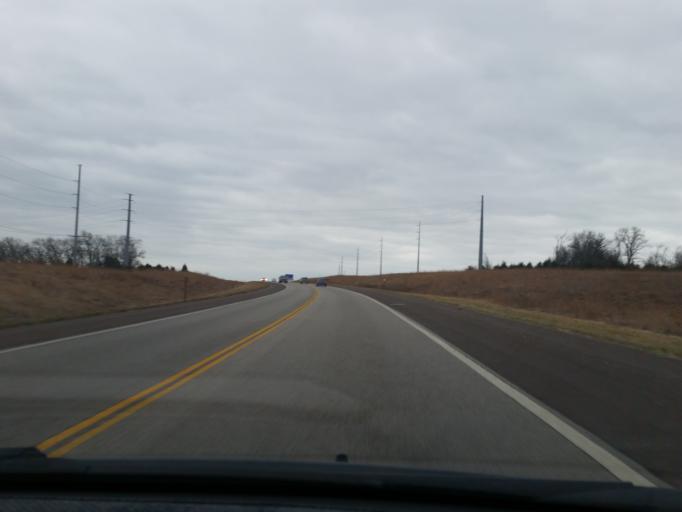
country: US
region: Kansas
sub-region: Douglas County
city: Lawrence
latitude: 38.9882
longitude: -95.3419
